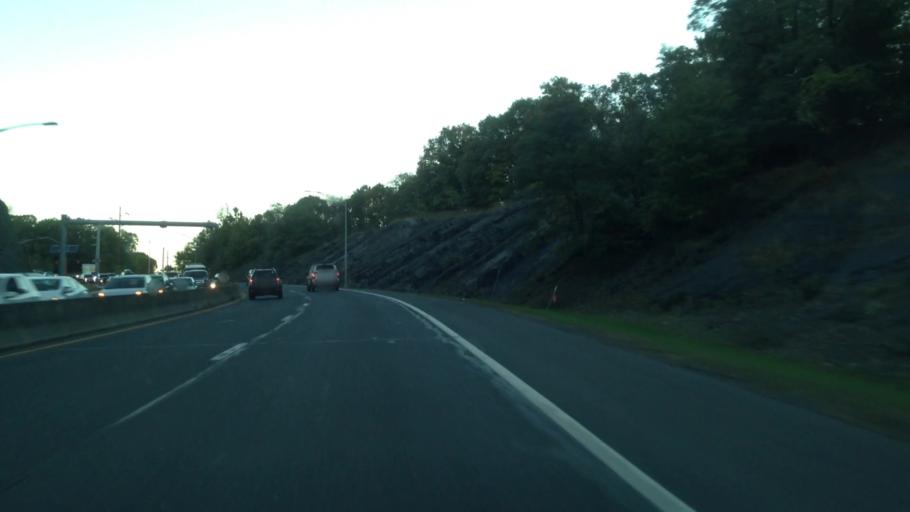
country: US
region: New York
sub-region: Ulster County
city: Highland
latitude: 41.7050
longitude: -73.9525
